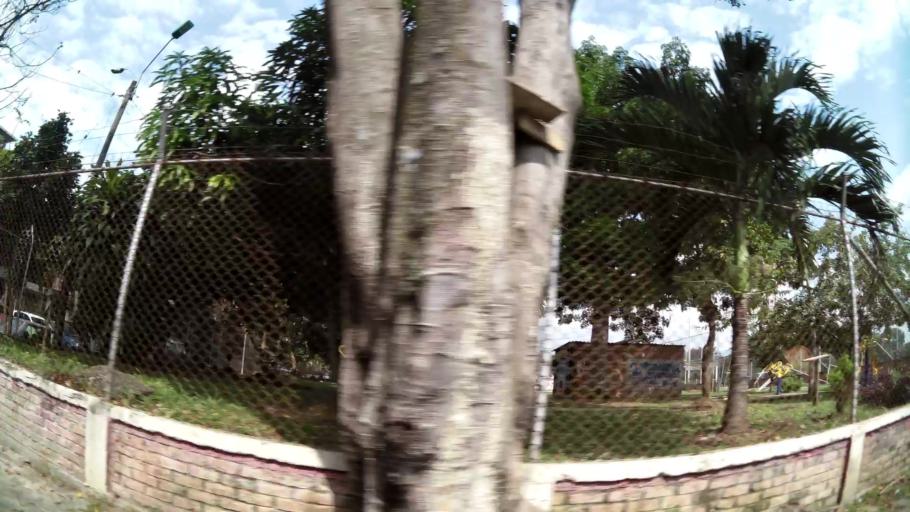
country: CO
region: Valle del Cauca
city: Cali
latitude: 3.4975
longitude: -76.4944
